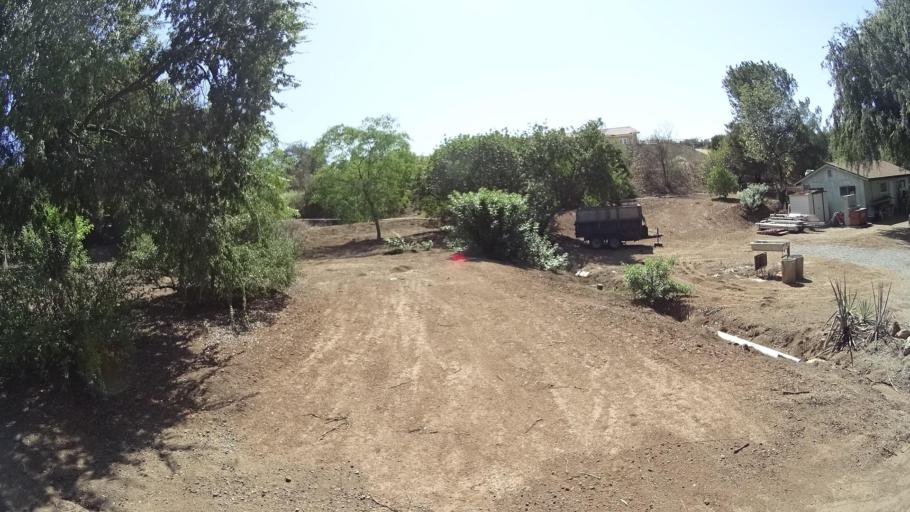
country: US
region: California
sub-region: San Diego County
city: Crest
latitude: 32.8227
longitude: -116.8543
